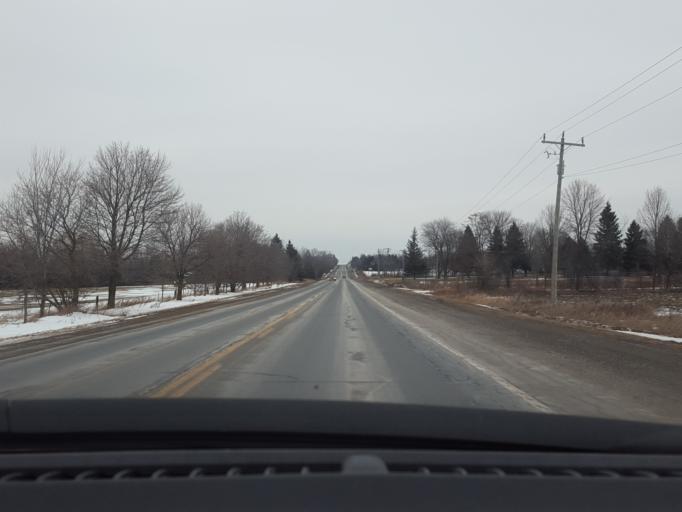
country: CA
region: Ontario
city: Newmarket
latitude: 44.1171
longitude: -79.4191
